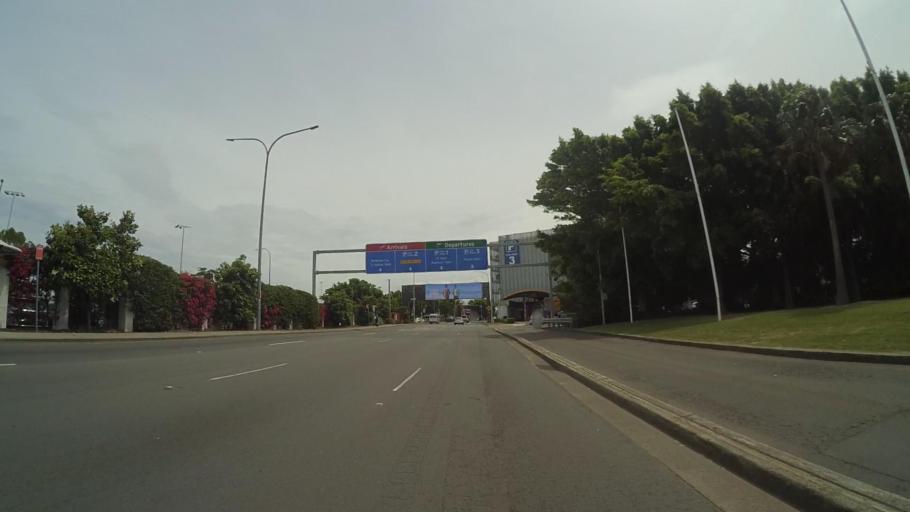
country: AU
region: New South Wales
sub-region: Botany Bay
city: Mascot
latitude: -33.9341
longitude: 151.1852
